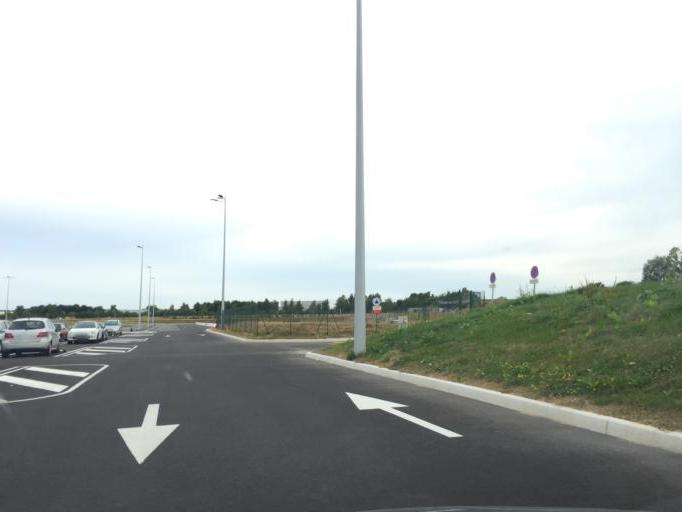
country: FR
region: Auvergne
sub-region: Departement de l'Allier
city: Moulins
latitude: 46.5886
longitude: 3.3320
